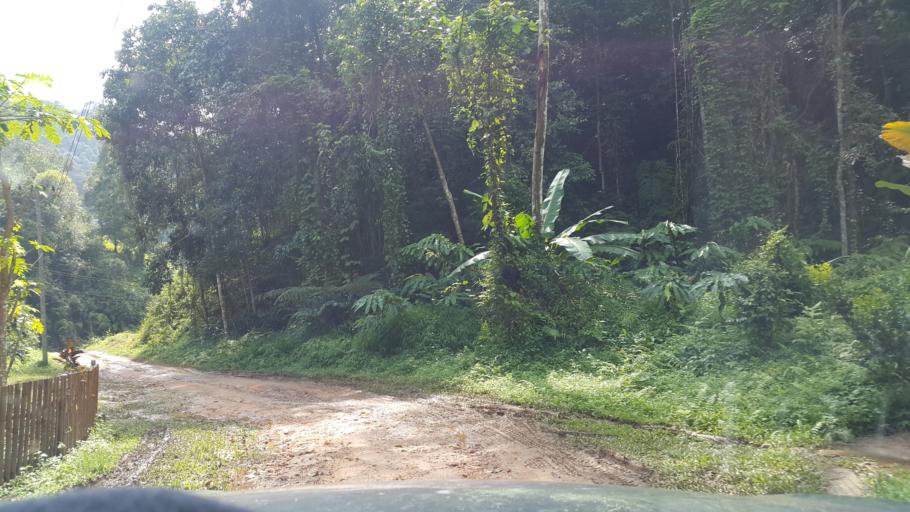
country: TH
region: Chiang Mai
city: Phrao
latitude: 19.1079
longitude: 99.2815
